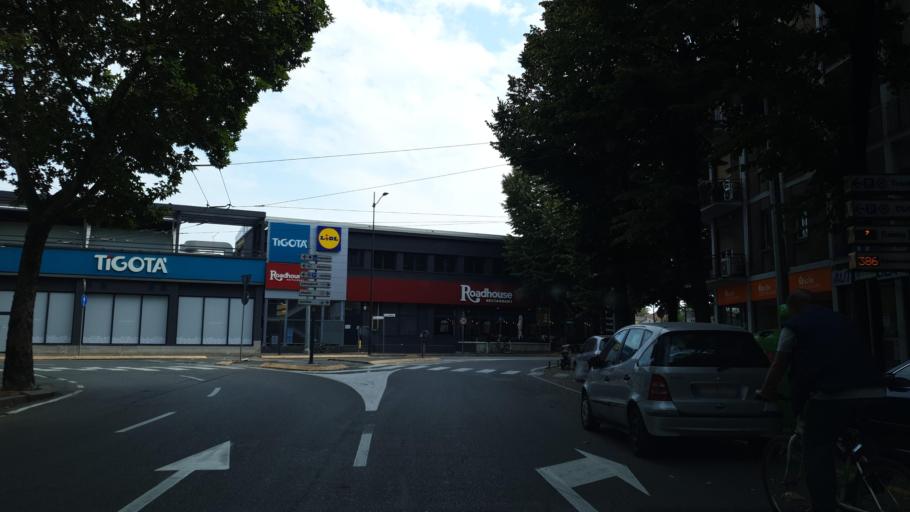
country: IT
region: Emilia-Romagna
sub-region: Provincia di Parma
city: Parma
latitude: 44.8058
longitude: 10.3041
